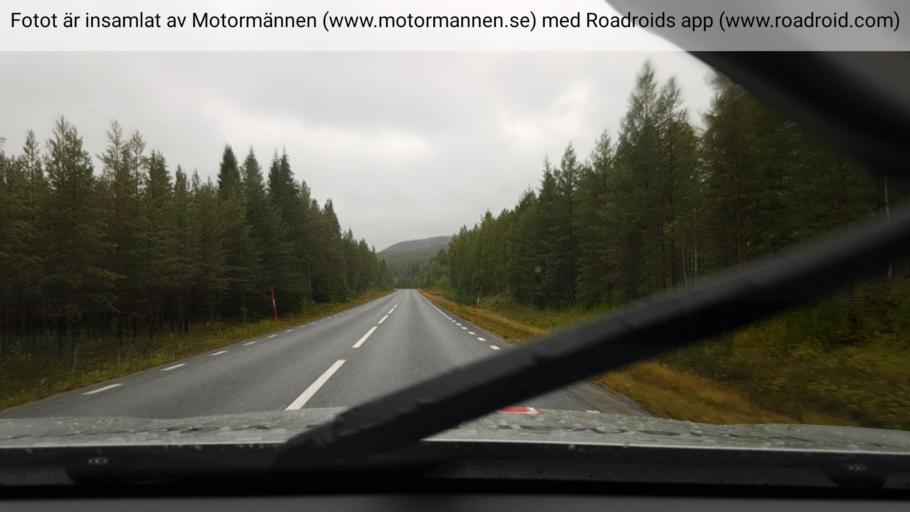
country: SE
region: Vaesterbotten
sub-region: Bjurholms Kommun
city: Bjurholm
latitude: 64.0194
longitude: 18.6737
